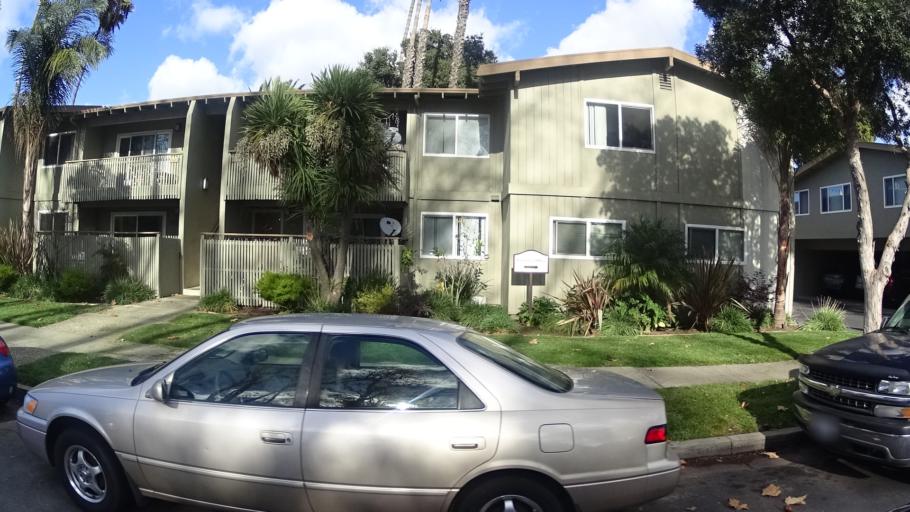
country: US
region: California
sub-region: Santa Clara County
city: Sunnyvale
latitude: 37.3842
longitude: -122.0540
